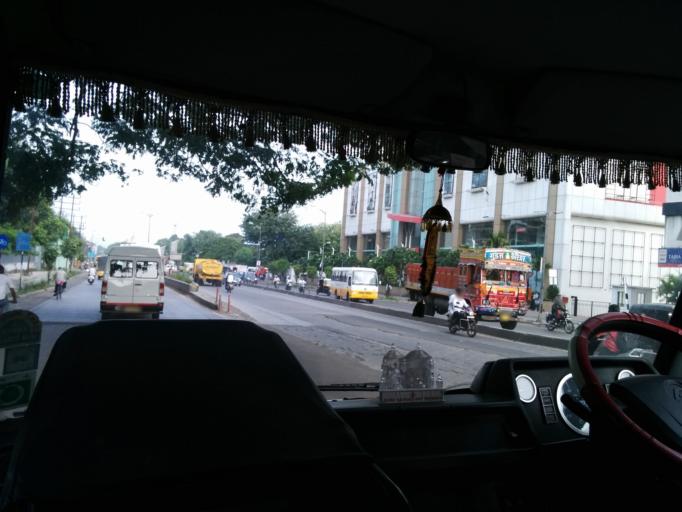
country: IN
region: Maharashtra
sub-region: Pune Division
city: Pune
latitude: 18.5063
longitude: 73.9083
